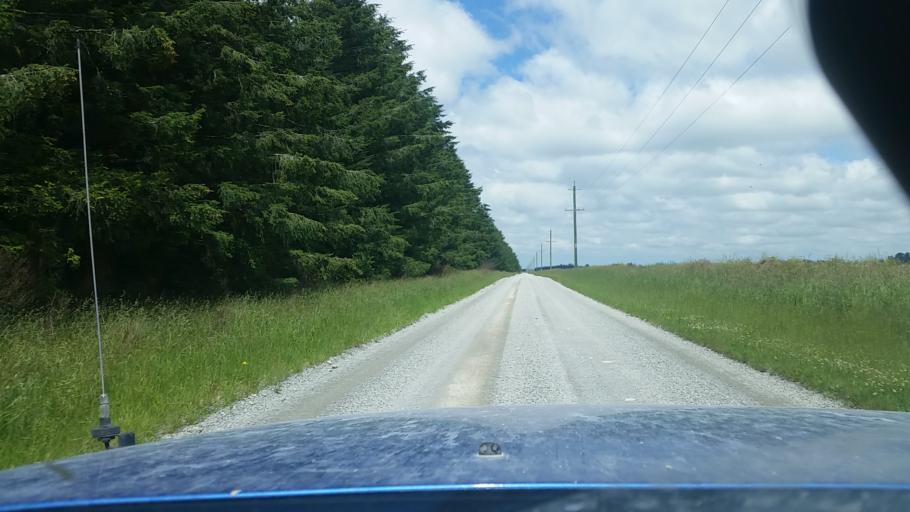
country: NZ
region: Canterbury
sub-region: Ashburton District
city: Tinwald
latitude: -43.8515
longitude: 171.3719
